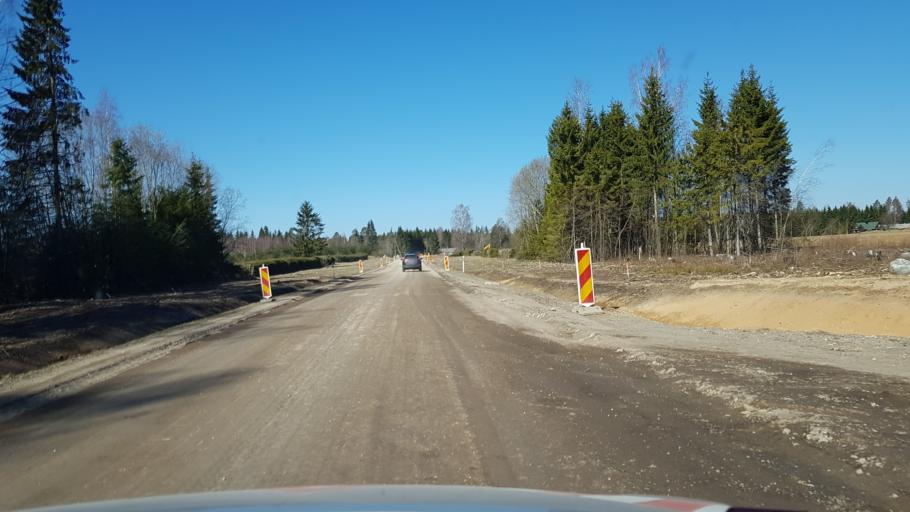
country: EE
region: Jogevamaa
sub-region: Mustvee linn
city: Mustvee
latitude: 59.0397
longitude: 26.6714
